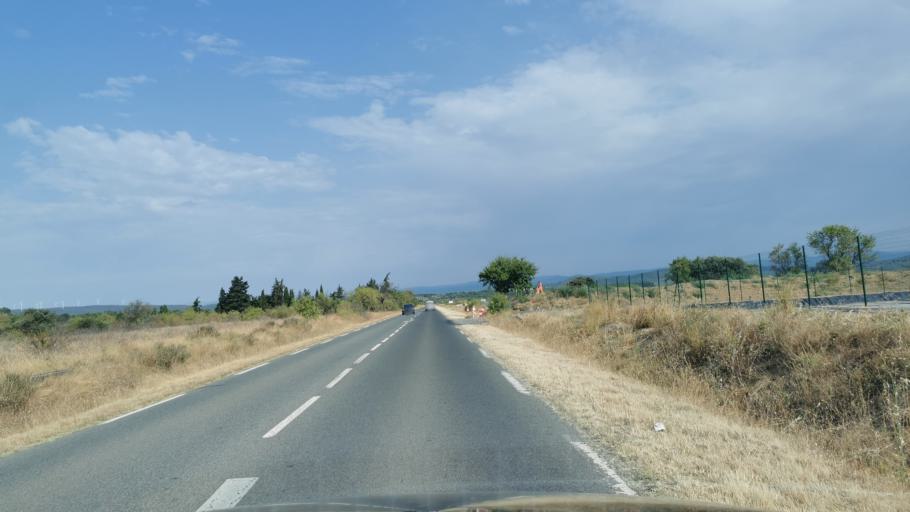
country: FR
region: Languedoc-Roussillon
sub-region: Departement de l'Aude
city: Ginestas
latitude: 43.2770
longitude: 2.8843
